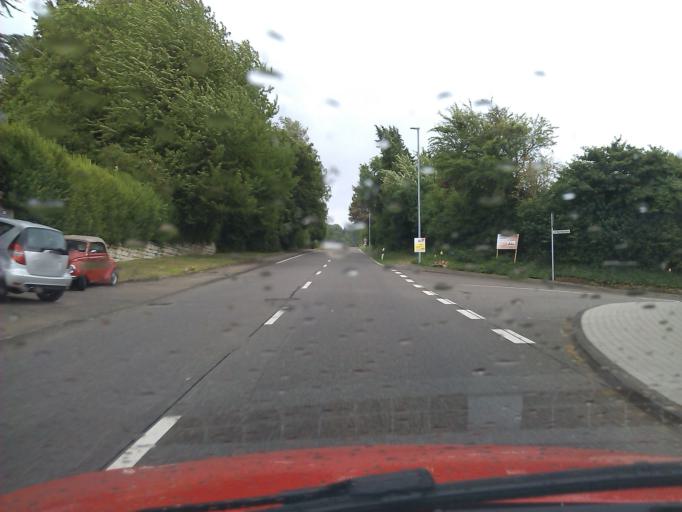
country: DE
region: Baden-Wuerttemberg
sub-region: Regierungsbezirk Stuttgart
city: Pfaffenhofen
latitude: 49.0962
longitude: 8.9770
